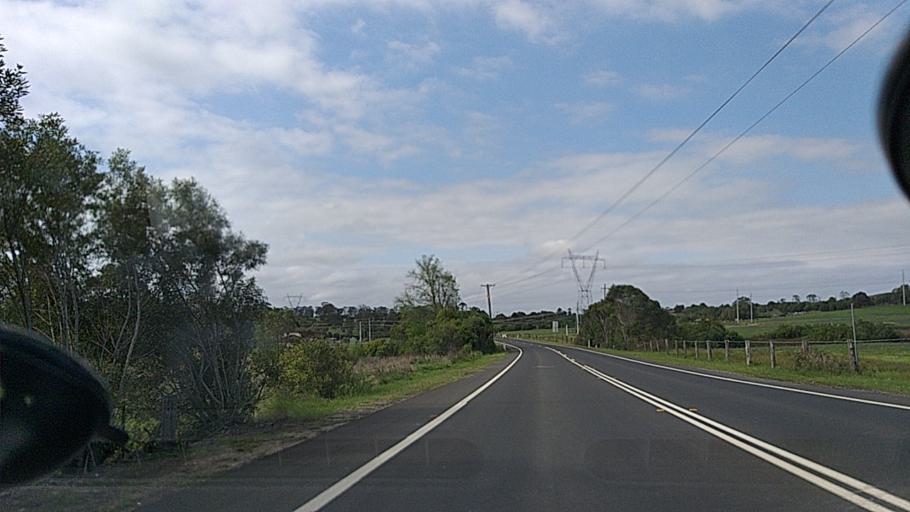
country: AU
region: New South Wales
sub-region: Campbelltown Municipality
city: Glen Alpine
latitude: -34.0974
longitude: 150.7672
